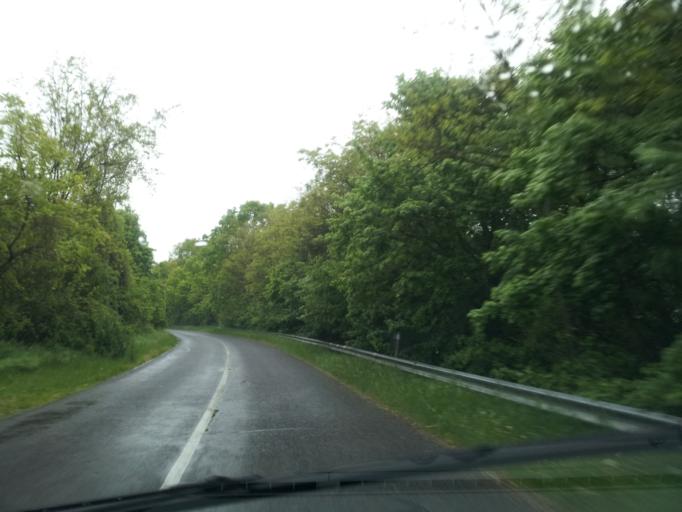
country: HU
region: Tolna
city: Bonyhad
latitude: 46.2564
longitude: 18.6078
